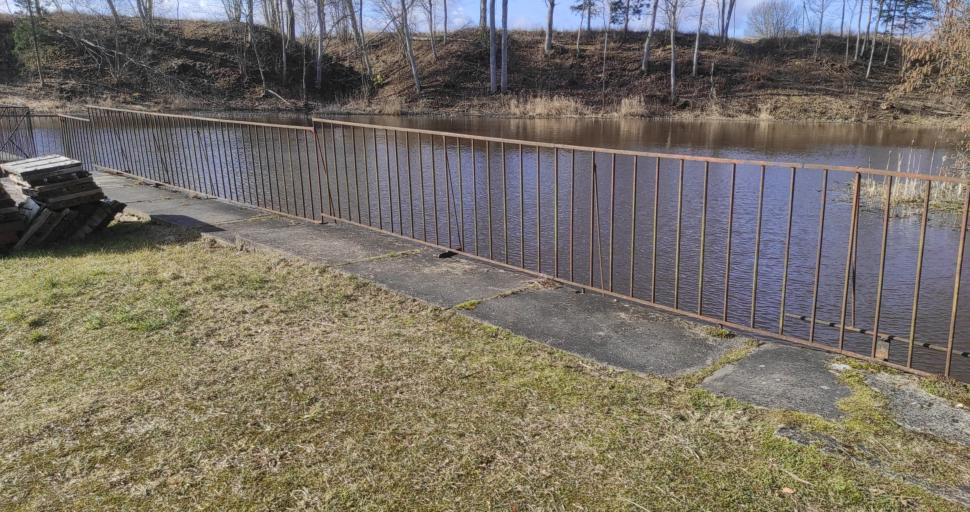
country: LV
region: Talsu Rajons
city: Valdemarpils
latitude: 57.4468
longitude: 22.6525
